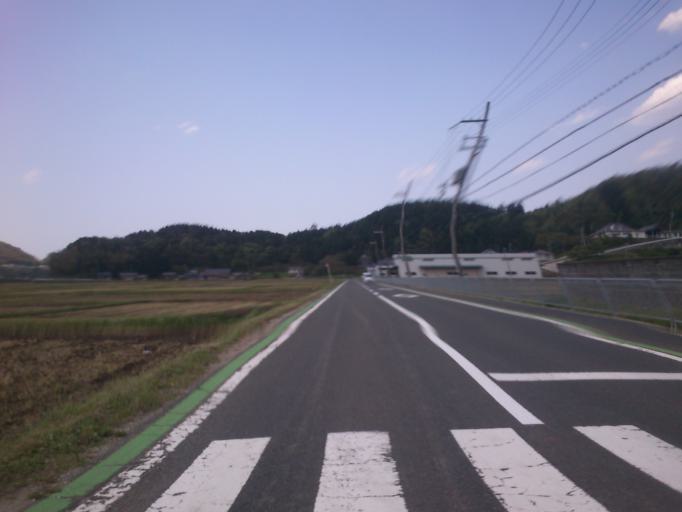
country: JP
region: Kyoto
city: Miyazu
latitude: 35.7222
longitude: 135.1073
